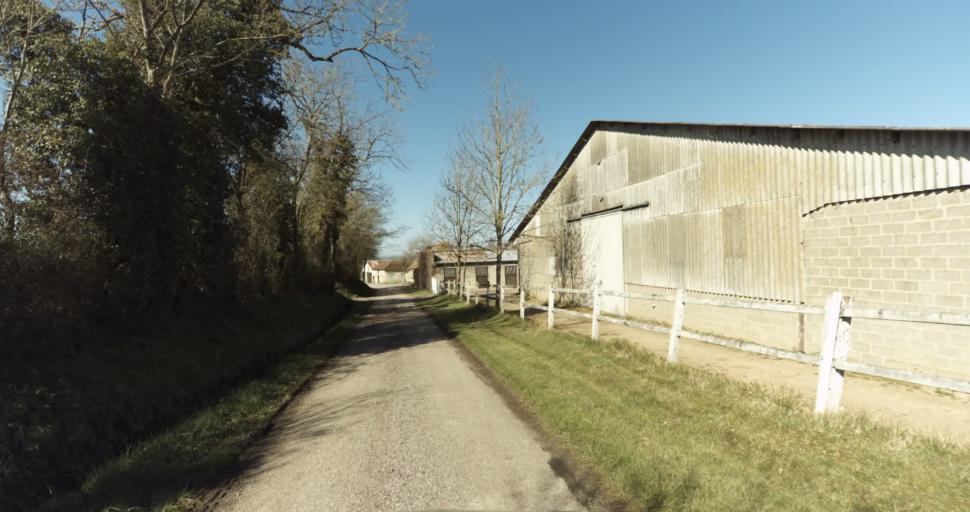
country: FR
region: Lower Normandy
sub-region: Departement de l'Orne
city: Trun
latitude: 48.9317
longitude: 0.0483
